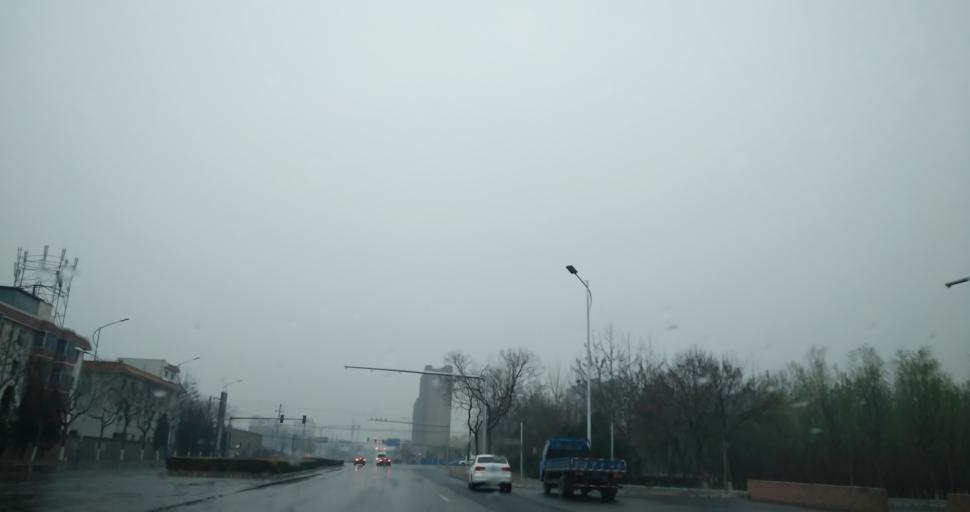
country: CN
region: Beijing
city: Yinghai
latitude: 39.7084
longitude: 116.4045
